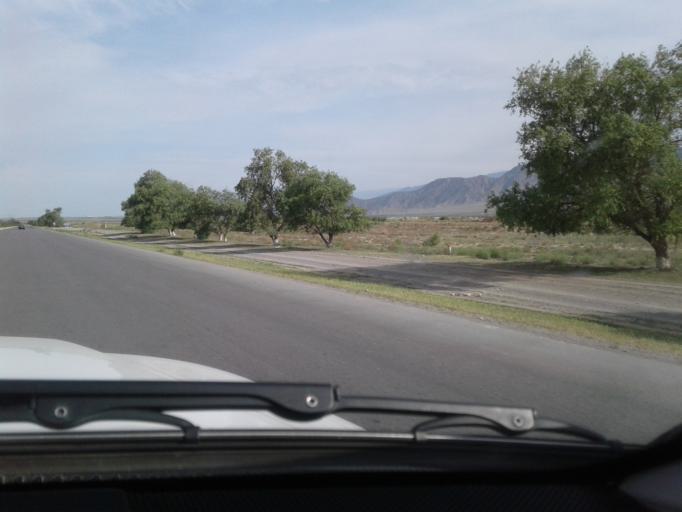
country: TM
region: Ahal
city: Arcabil
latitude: 38.1895
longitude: 57.8461
